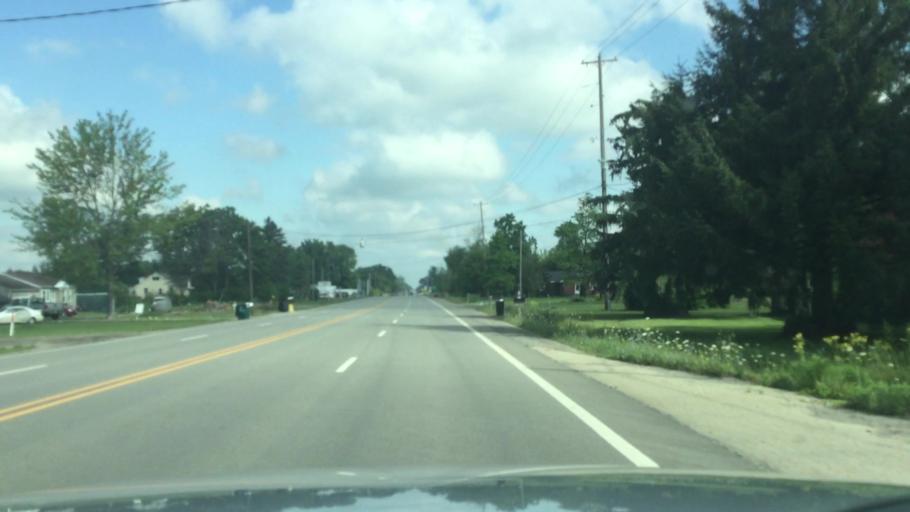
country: US
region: Michigan
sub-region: Genesee County
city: Clio
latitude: 43.1985
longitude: -83.7303
